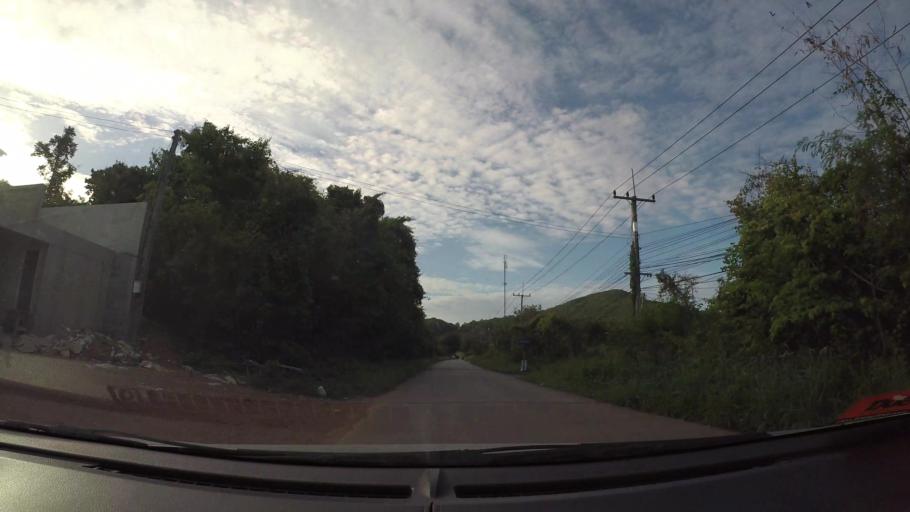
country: TH
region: Chon Buri
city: Sattahip
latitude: 12.6803
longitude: 100.9273
